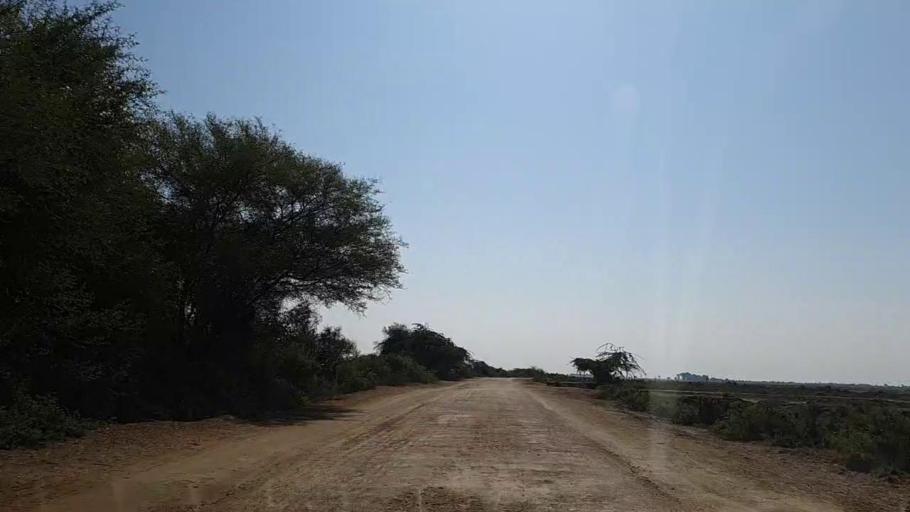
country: PK
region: Sindh
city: Chuhar Jamali
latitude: 24.5124
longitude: 68.0970
